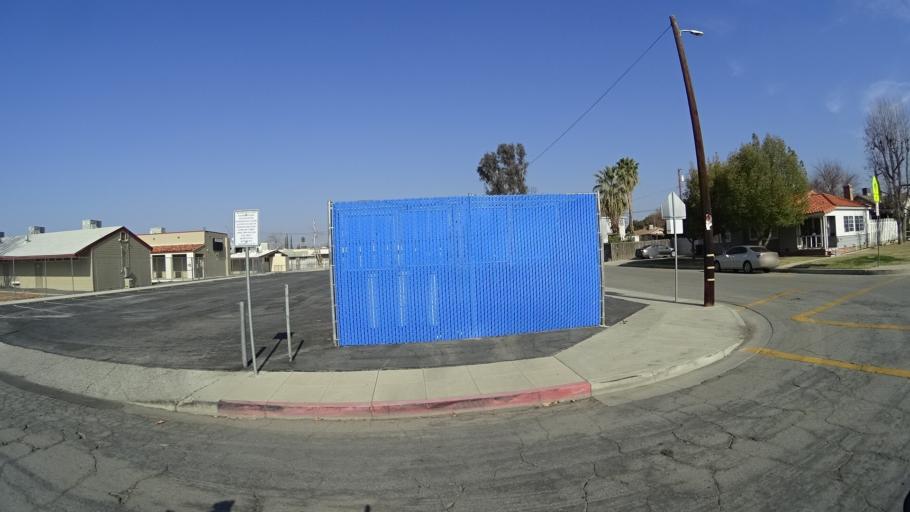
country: US
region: California
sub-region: Kern County
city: Bakersfield
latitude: 35.3884
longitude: -119.0009
